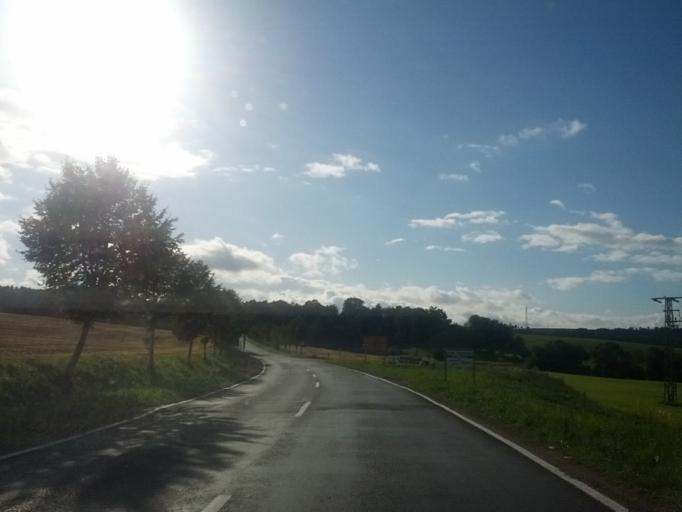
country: DE
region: Thuringia
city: Marksuhl
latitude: 50.9507
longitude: 10.1772
